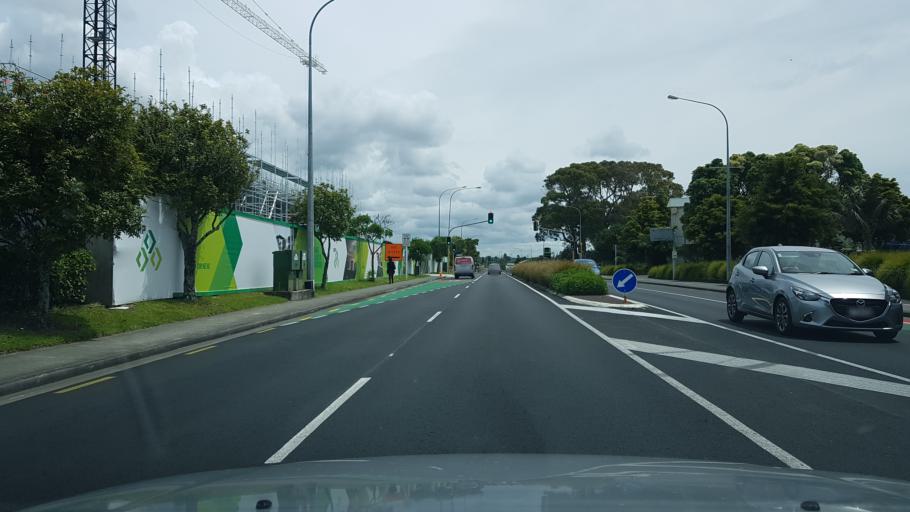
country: NZ
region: Auckland
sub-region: Auckland
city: North Shore
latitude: -36.7990
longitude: 174.7570
